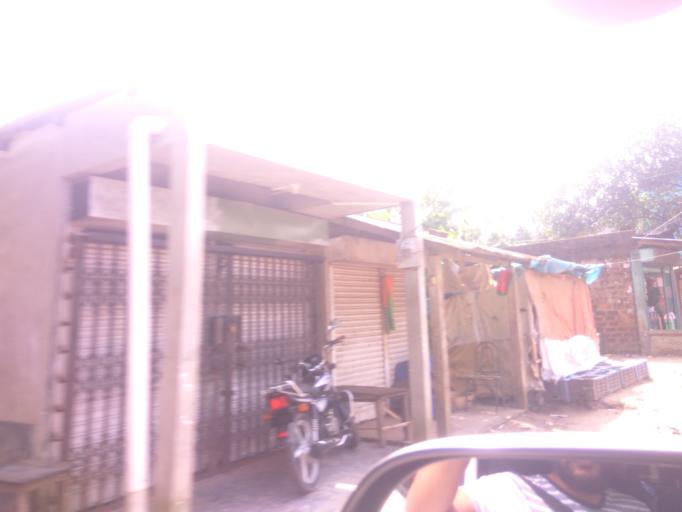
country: IN
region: Assam
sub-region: Karimganj
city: Karimganj
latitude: 24.8094
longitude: 92.1831
